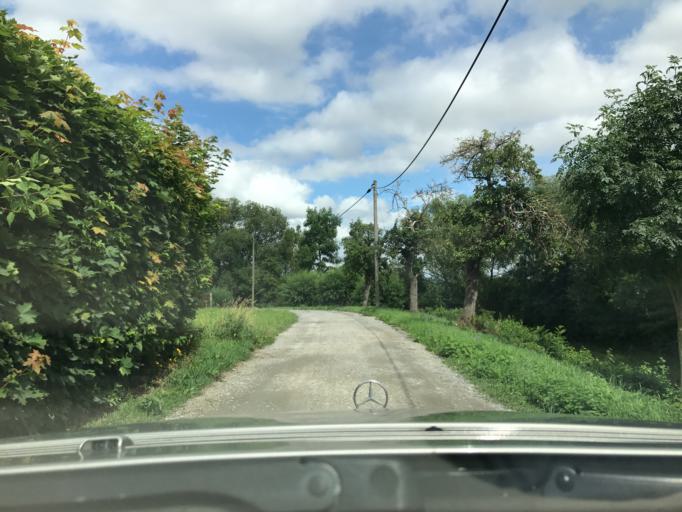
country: DE
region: Thuringia
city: Muehlhausen
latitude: 51.2208
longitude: 10.4351
